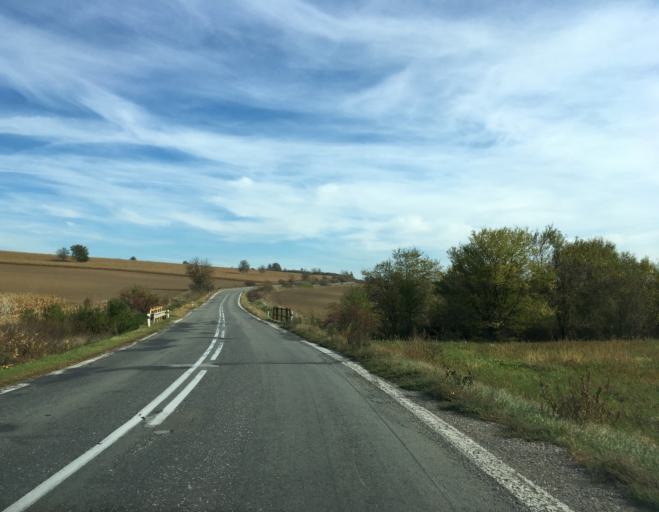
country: SK
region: Nitriansky
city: Svodin
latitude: 48.0324
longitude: 18.4519
